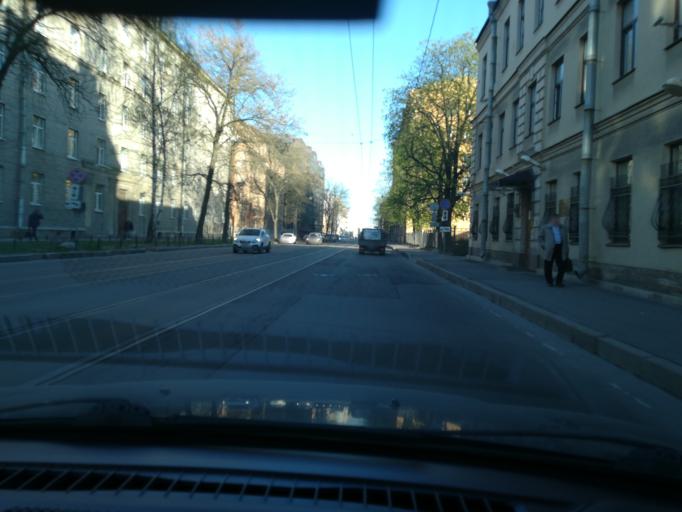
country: RU
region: St.-Petersburg
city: Vasyl'evsky Ostrov
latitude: 59.9353
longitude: 30.2601
